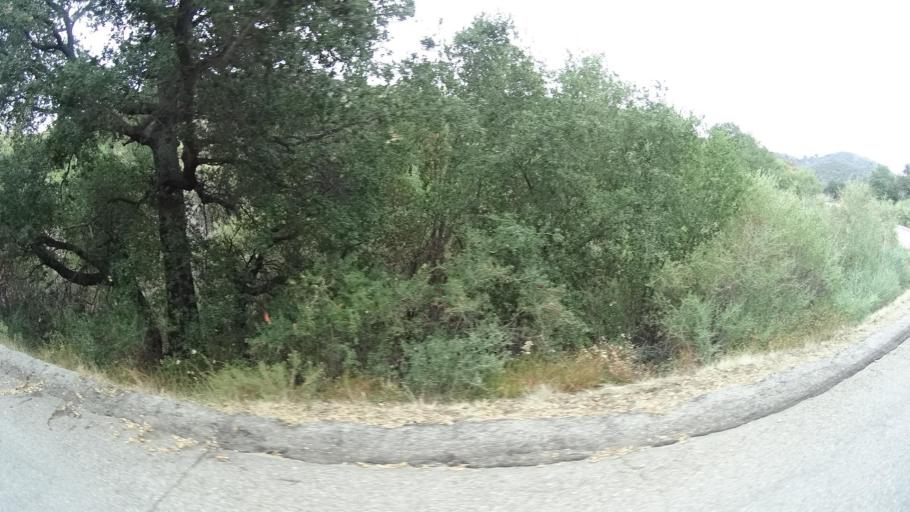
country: US
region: California
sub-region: San Diego County
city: San Diego Country Estates
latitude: 32.9689
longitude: -116.6709
